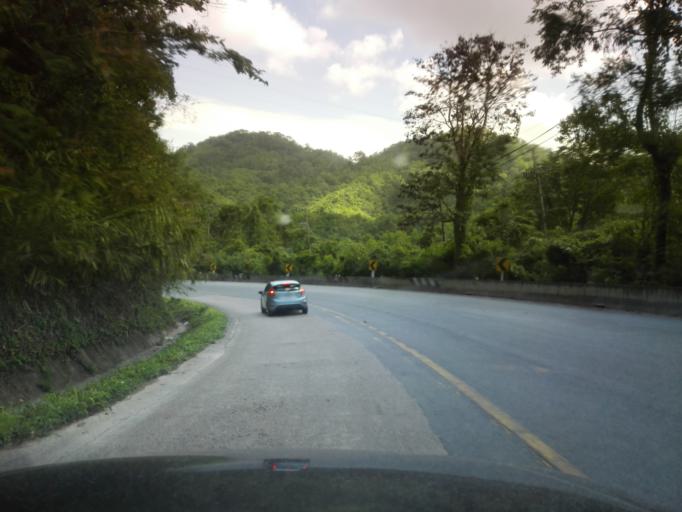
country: TH
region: Tak
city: Mae Sot
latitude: 16.7622
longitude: 98.7121
